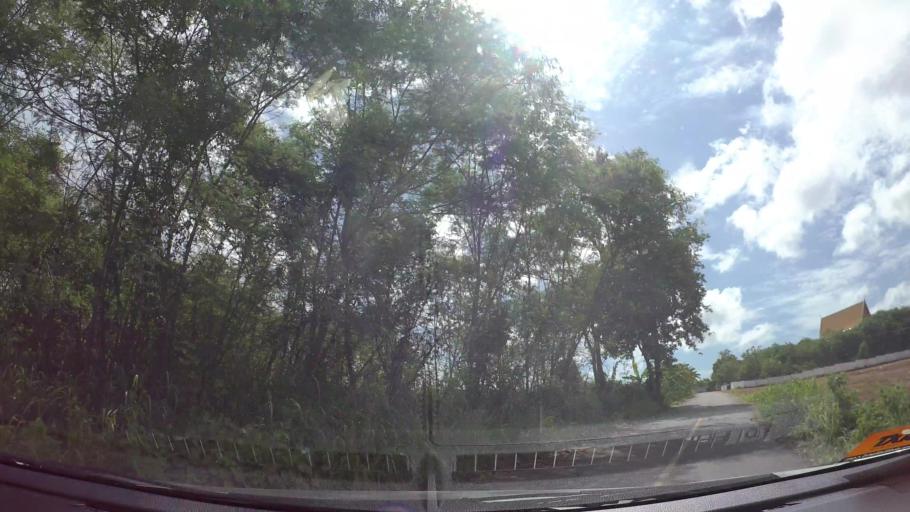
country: TH
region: Chon Buri
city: Sattahip
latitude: 12.6921
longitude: 100.9047
